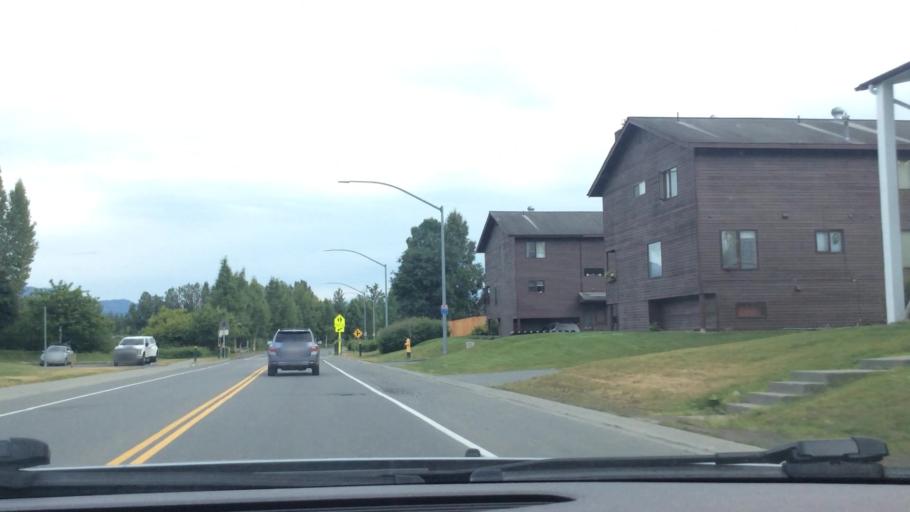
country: US
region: Alaska
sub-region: Anchorage Municipality
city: Anchorage
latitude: 61.2032
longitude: -149.7625
